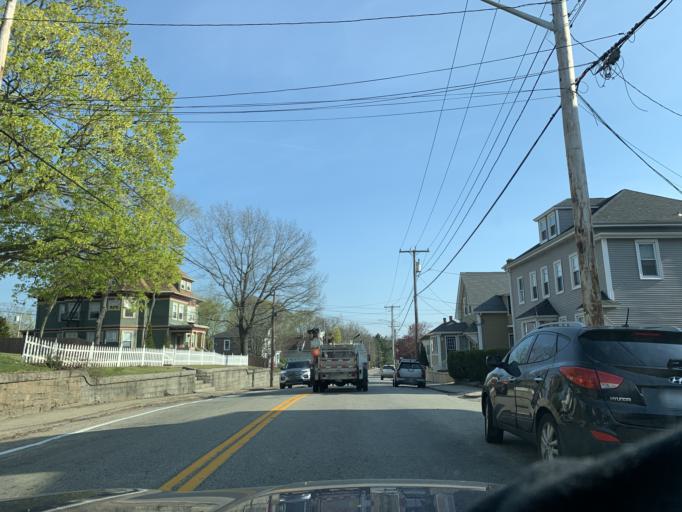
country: US
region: Rhode Island
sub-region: Kent County
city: West Warwick
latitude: 41.6995
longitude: -71.5224
